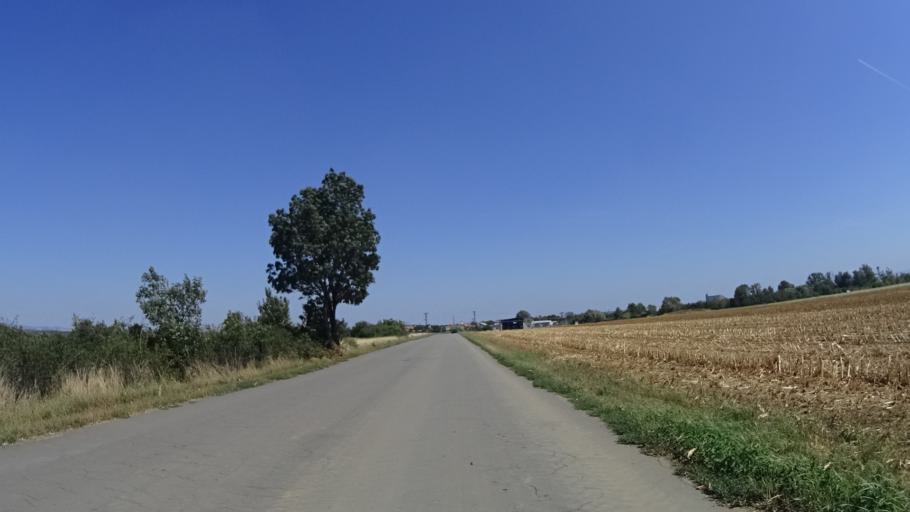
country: CZ
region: South Moravian
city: Petrov
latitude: 48.8893
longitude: 17.2947
